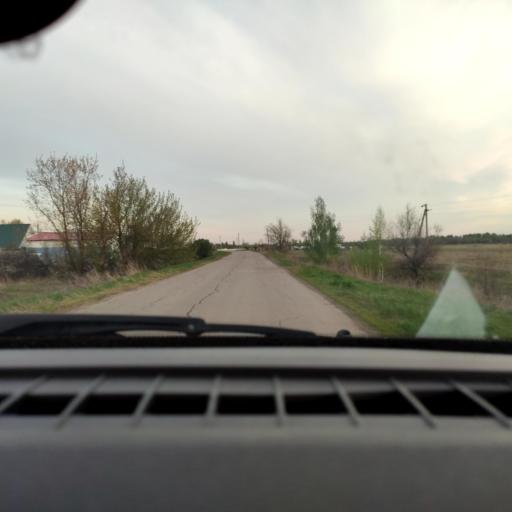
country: RU
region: Samara
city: Georgiyevka
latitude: 53.2720
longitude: 50.9574
